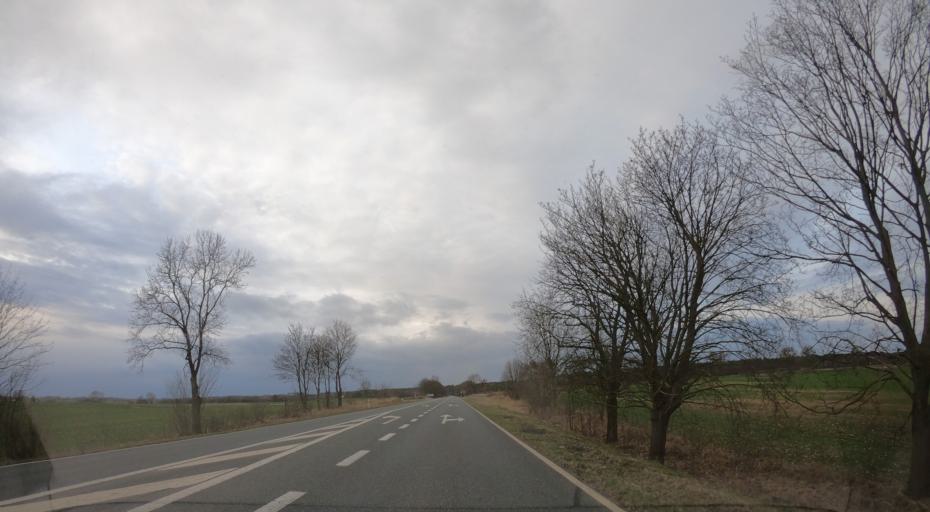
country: PL
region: West Pomeranian Voivodeship
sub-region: Powiat mysliborski
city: Nowogrodek Pomorski
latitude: 52.9090
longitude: 14.9719
